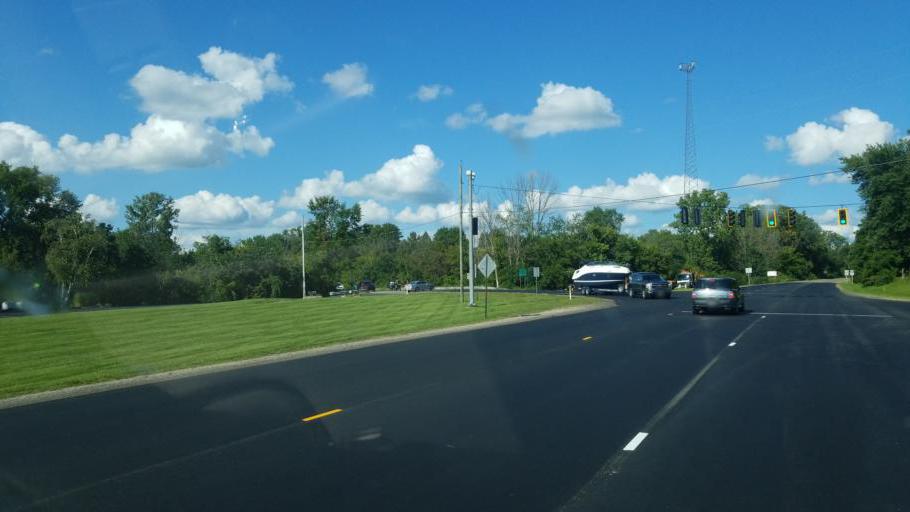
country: US
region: Ohio
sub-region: Delaware County
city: Sunbury
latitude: 40.2491
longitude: -82.8591
